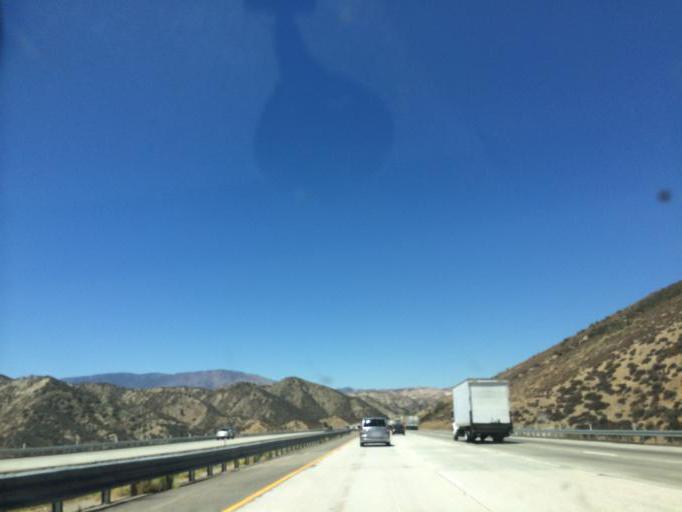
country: US
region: California
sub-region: Kern County
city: Lebec
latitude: 34.6832
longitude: -118.7822
